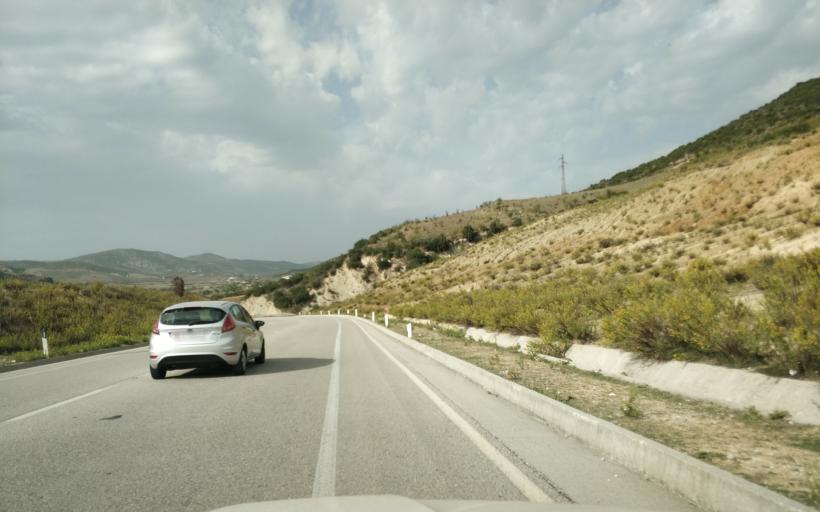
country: AL
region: Gjirokaster
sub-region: Rrethi i Tepelenes
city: Krahes
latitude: 40.4016
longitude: 19.8636
